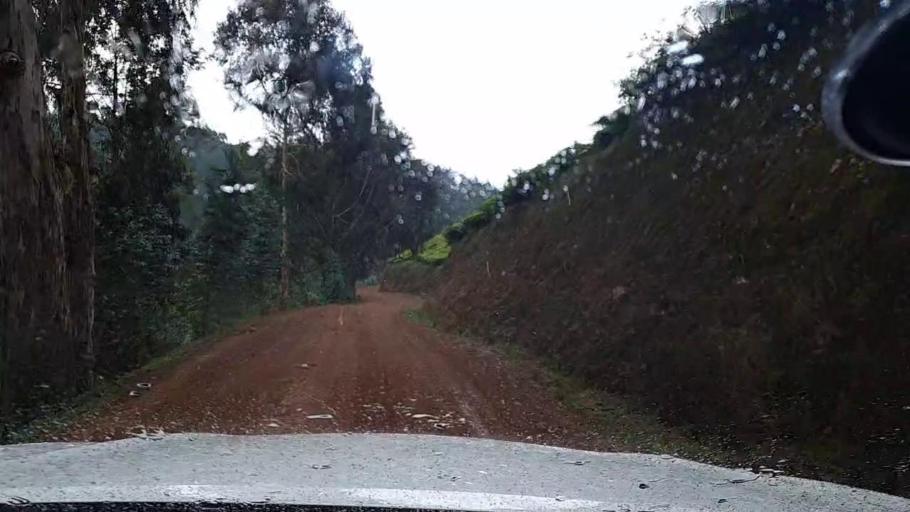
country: RW
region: Western Province
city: Kibuye
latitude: -2.1638
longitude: 29.4351
